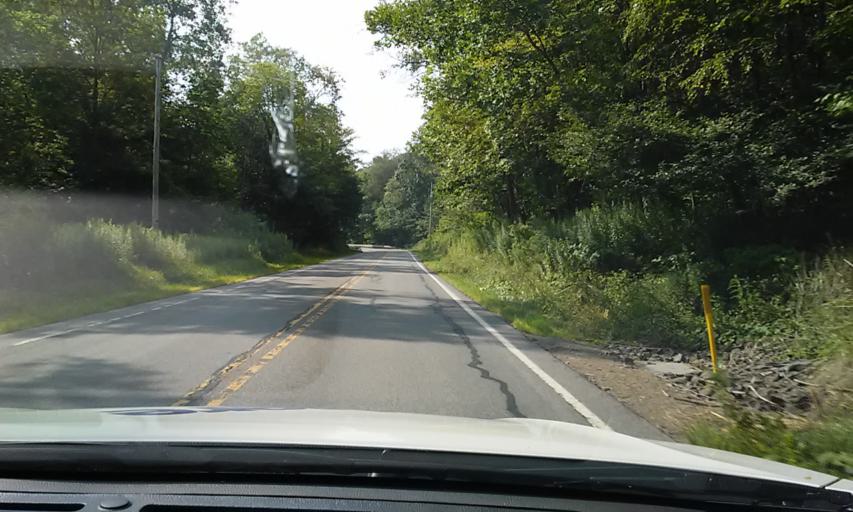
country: US
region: Pennsylvania
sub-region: Potter County
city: Galeton
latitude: 41.8585
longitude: -77.8178
